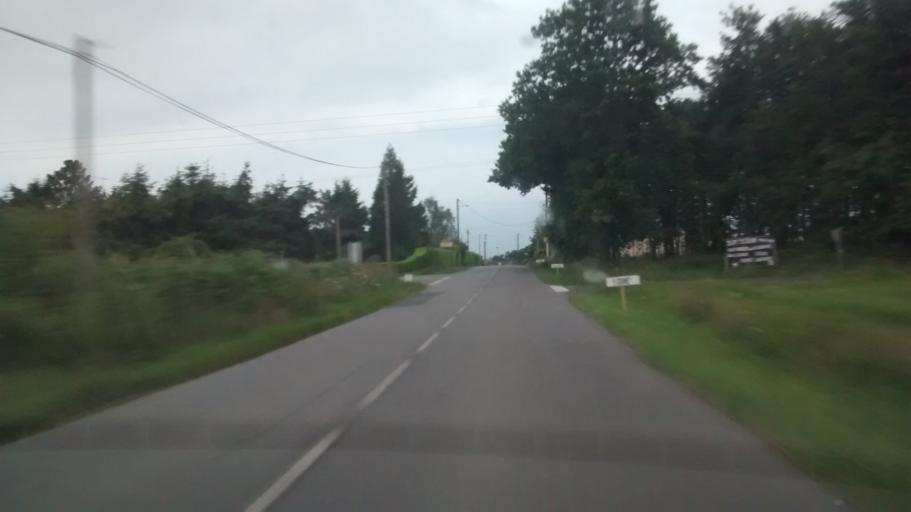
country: FR
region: Brittany
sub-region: Departement du Morbihan
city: Saint-Martin-sur-Oust
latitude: 47.7288
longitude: -2.2796
